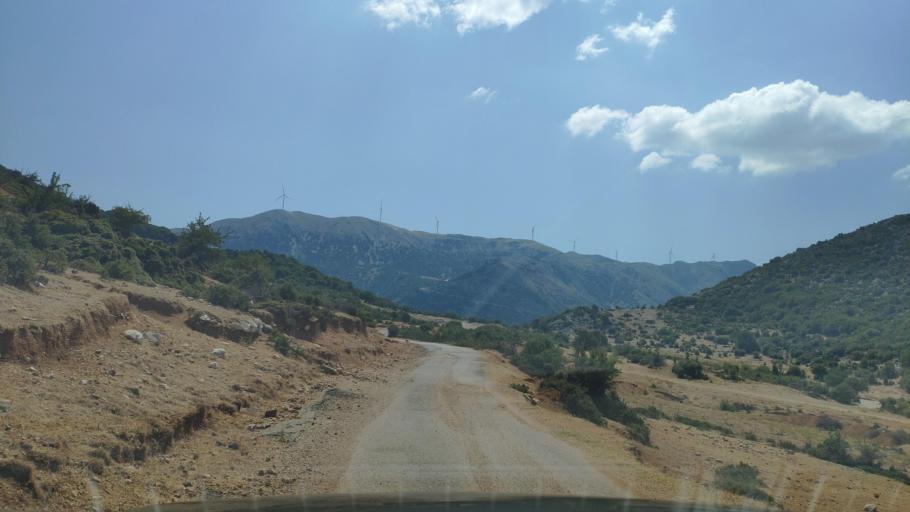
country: GR
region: West Greece
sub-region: Nomos Aitolias kai Akarnanias
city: Monastirakion
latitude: 38.7978
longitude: 20.9526
